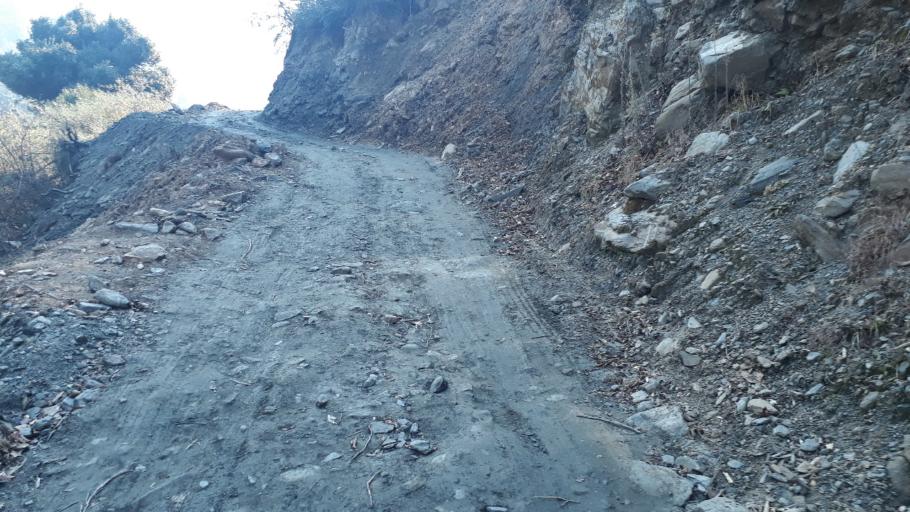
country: IN
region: Himachal Pradesh
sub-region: Mandi
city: Pandoh
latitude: 31.7767
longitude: 77.0866
